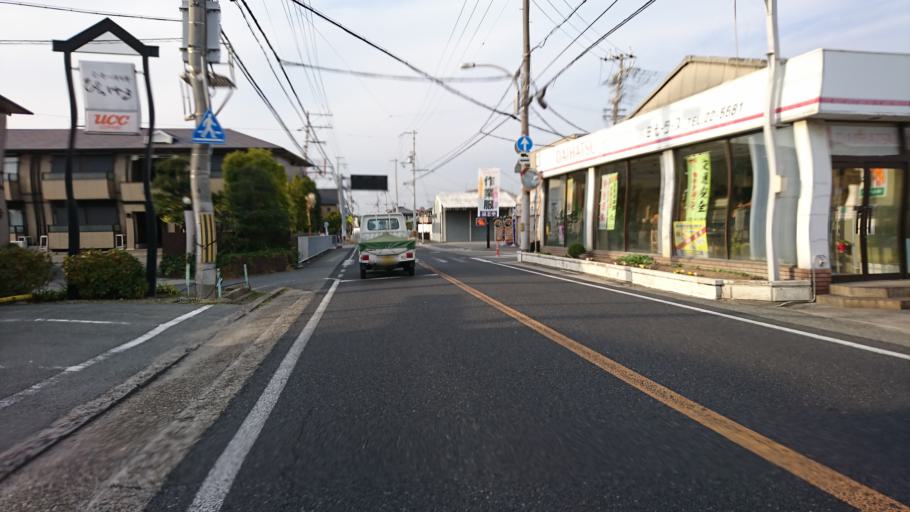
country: JP
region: Hyogo
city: Kakogawacho-honmachi
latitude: 34.7450
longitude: 134.8196
